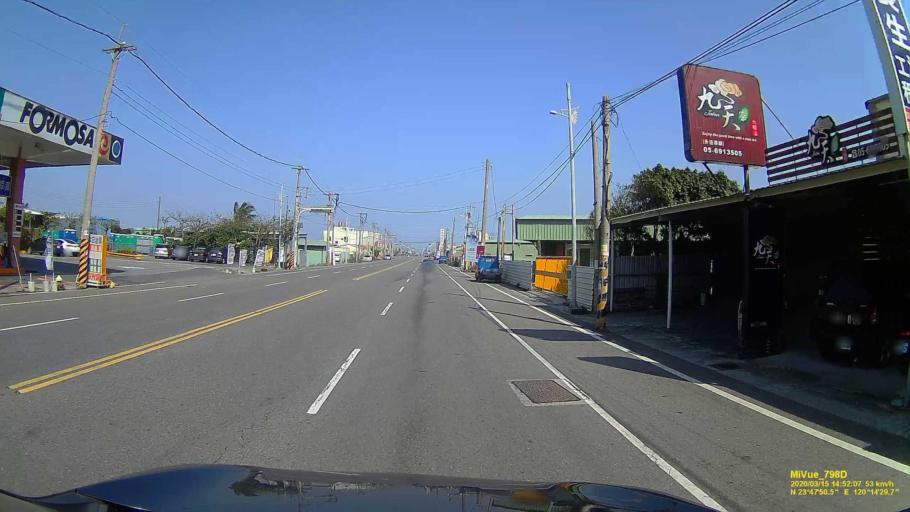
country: TW
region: Taiwan
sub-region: Yunlin
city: Douliu
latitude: 23.7974
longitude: 120.2418
